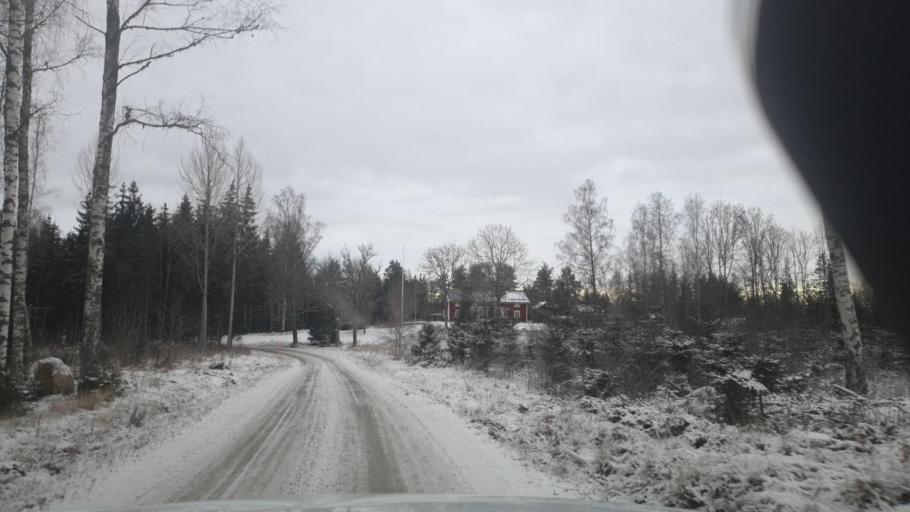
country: SE
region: Vaermland
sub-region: Arvika Kommun
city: Arvika
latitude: 59.5655
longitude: 12.8355
